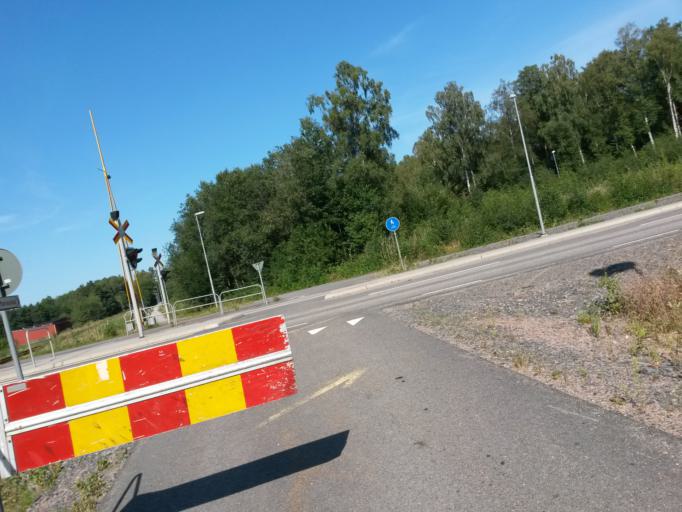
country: SE
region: Vaestra Goetaland
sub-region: Gotene Kommun
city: Kallby
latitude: 58.5035
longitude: 13.2943
